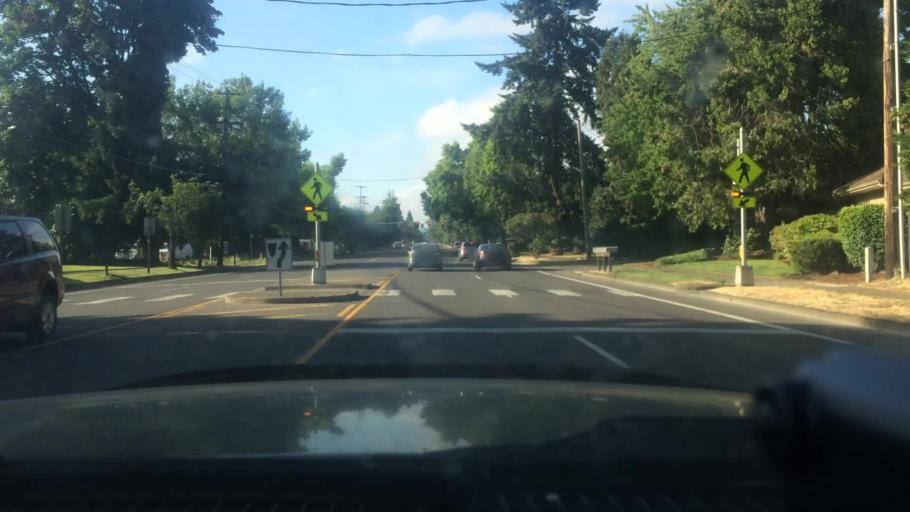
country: US
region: Oregon
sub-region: Lane County
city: Eugene
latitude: 44.0920
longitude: -123.1266
